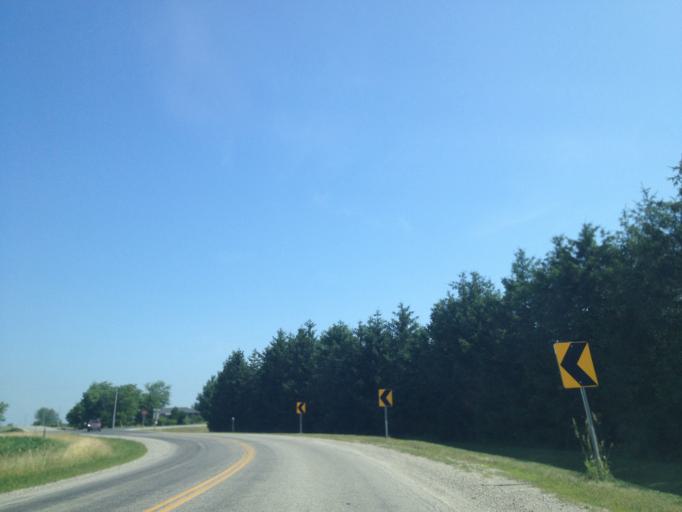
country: CA
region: Ontario
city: London
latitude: 43.1971
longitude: -81.2413
